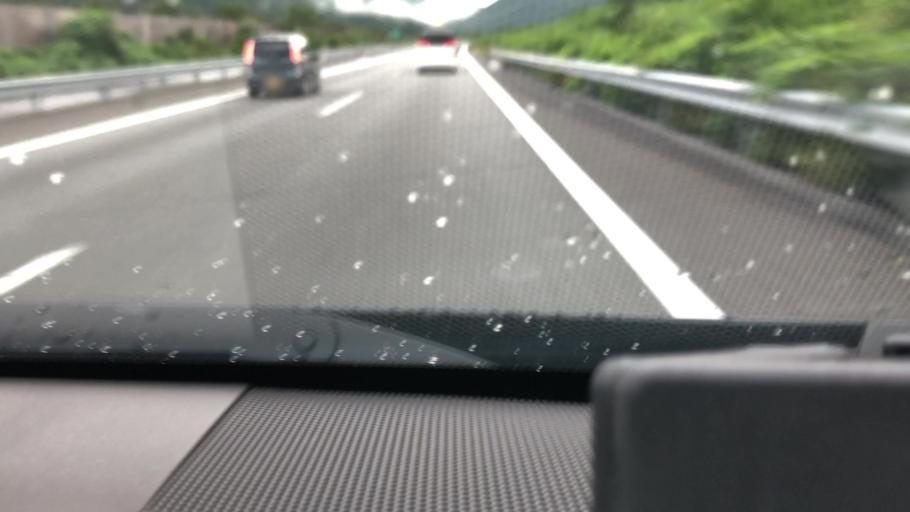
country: JP
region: Shizuoka
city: Mori
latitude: 34.8405
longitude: 137.9883
